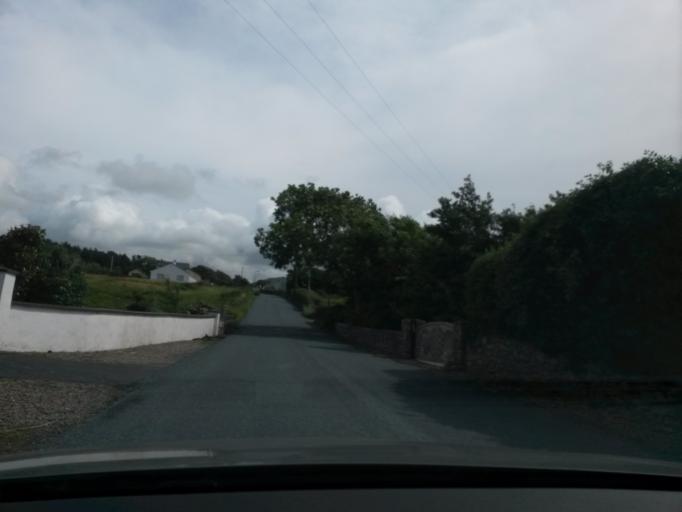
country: IE
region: Connaught
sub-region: Sligo
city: Sligo
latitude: 54.4335
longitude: -8.4577
